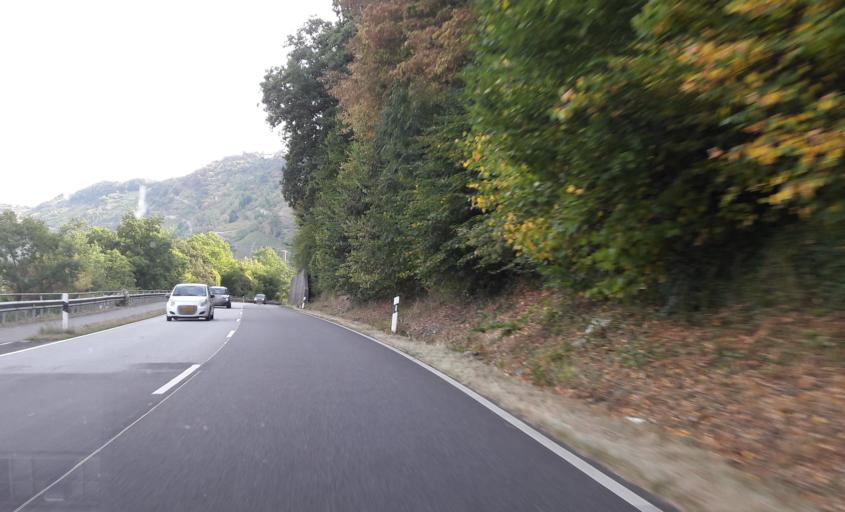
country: DE
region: Rheinland-Pfalz
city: Traben-Trarbach
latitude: 49.9493
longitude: 7.1266
